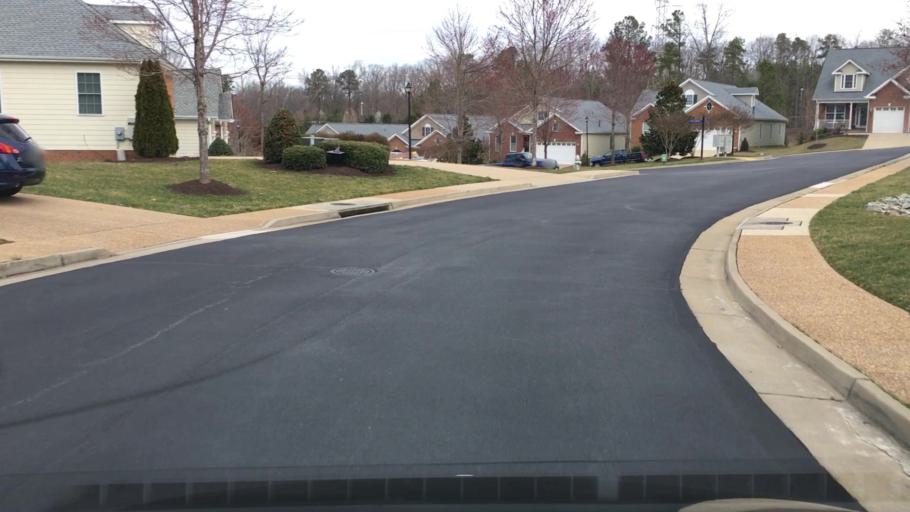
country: US
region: Virginia
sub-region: Chesterfield County
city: Bon Air
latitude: 37.5428
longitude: -77.5577
